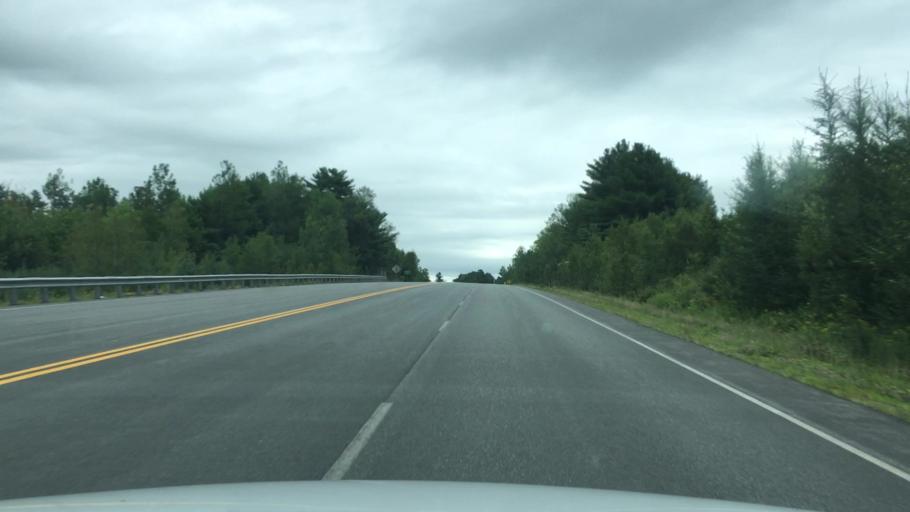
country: US
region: Maine
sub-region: Hancock County
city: Franklin
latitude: 44.8477
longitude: -68.3361
